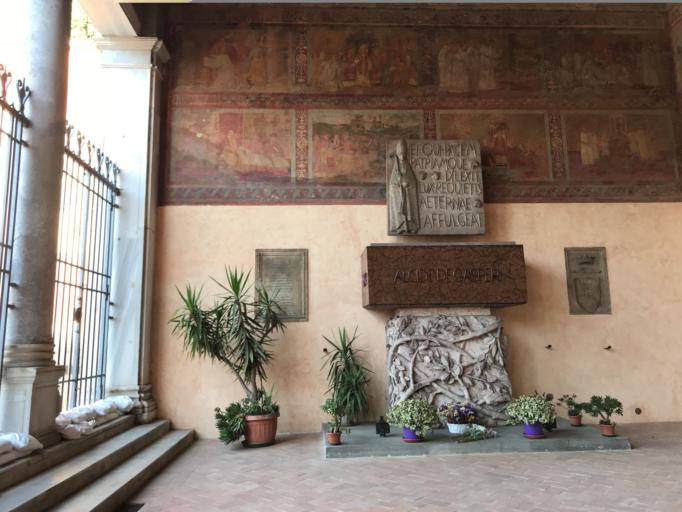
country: IT
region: Latium
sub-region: Citta metropolitana di Roma Capitale
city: Rome
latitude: 41.9025
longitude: 12.5204
